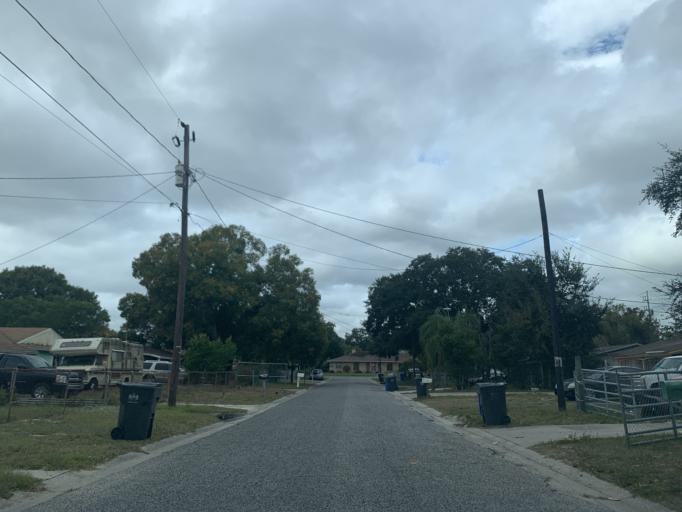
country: US
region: Florida
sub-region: Hillsborough County
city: East Lake-Orient Park
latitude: 27.9771
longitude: -82.3925
